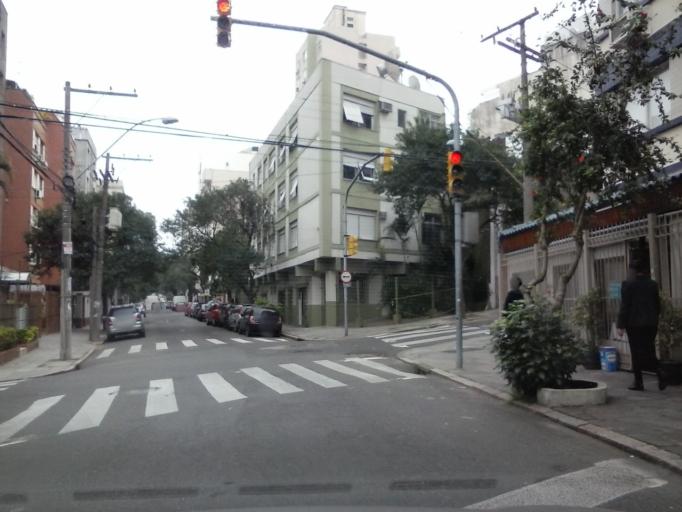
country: BR
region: Rio Grande do Sul
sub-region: Porto Alegre
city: Porto Alegre
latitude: -30.0349
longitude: -51.2336
